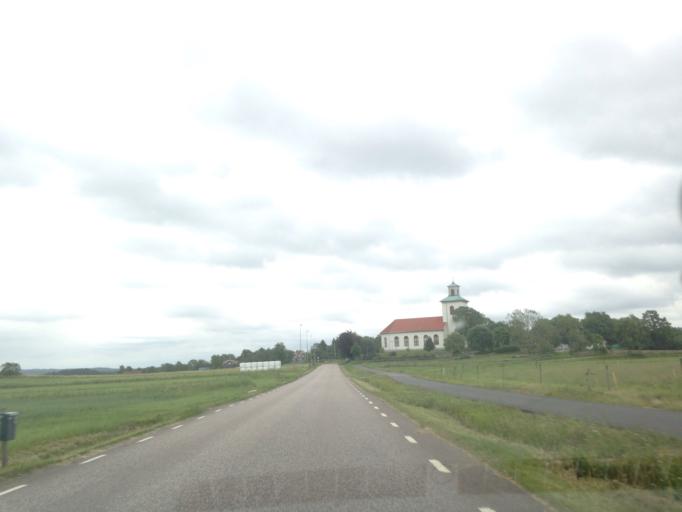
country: SE
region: Vaestra Goetaland
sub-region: Goteborg
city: Torslanda
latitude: 57.8187
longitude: 11.8345
